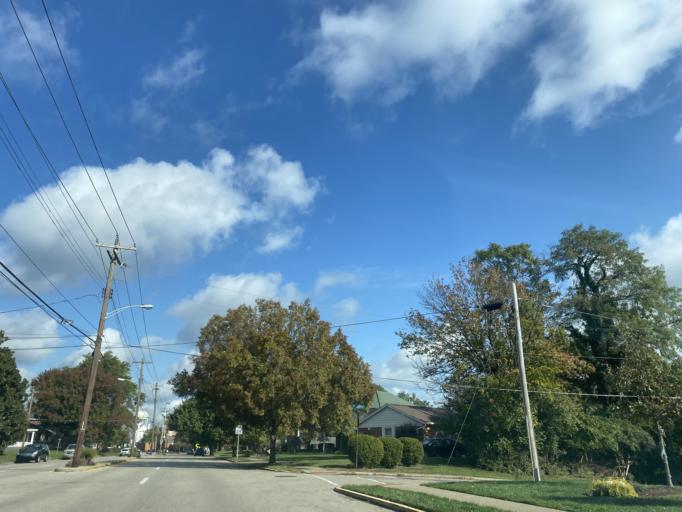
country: US
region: Kentucky
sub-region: Campbell County
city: Fort Thomas
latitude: 39.0744
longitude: -84.4471
